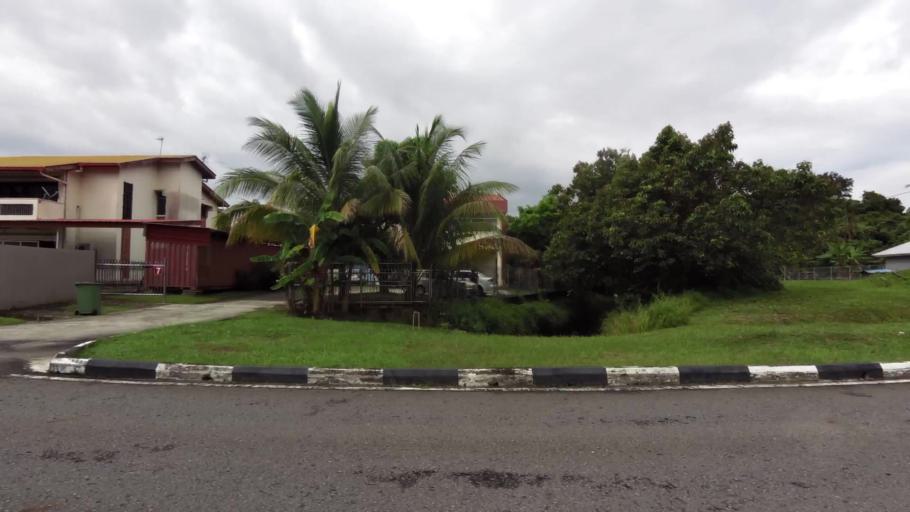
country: BN
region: Brunei and Muara
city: Bandar Seri Begawan
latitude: 4.9057
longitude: 114.9401
